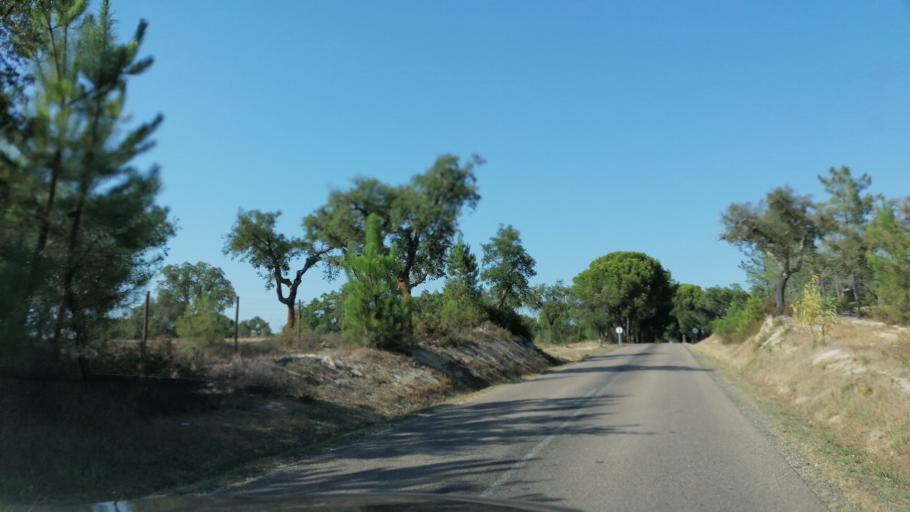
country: PT
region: Santarem
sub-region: Coruche
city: Coruche
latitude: 38.8105
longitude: -8.5767
